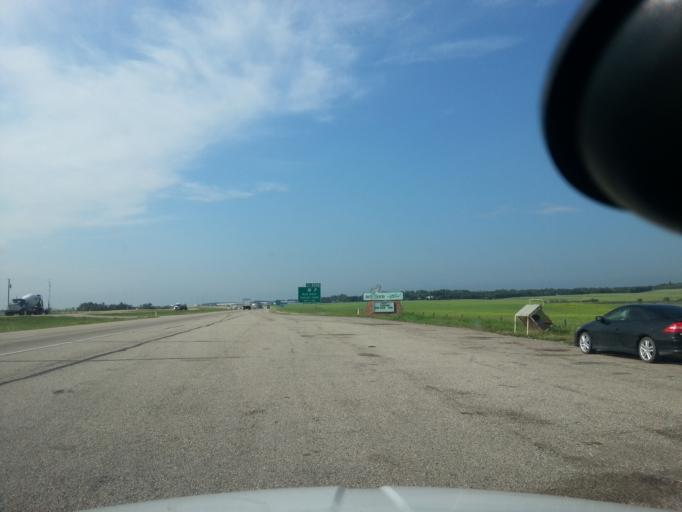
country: CA
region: Alberta
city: Red Deer
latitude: 52.3328
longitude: -113.8556
